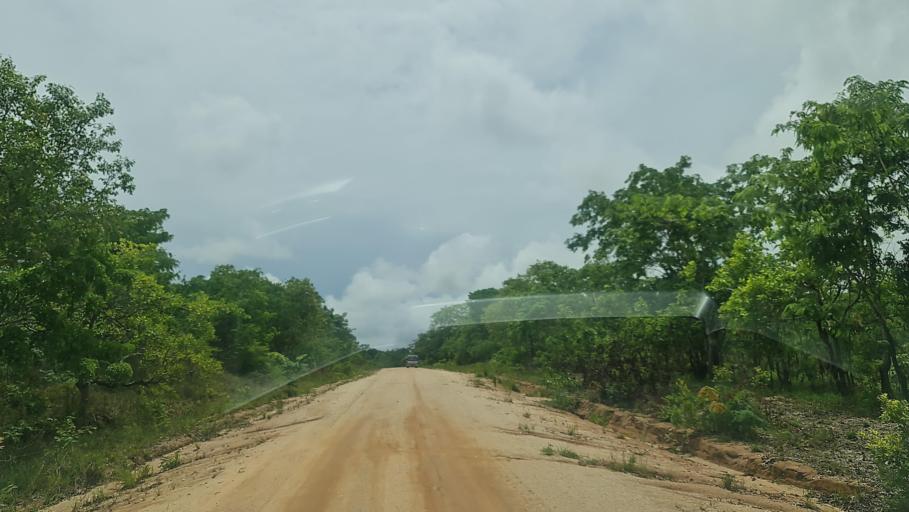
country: MZ
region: Zambezia
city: Quelimane
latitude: -17.2698
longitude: 37.2553
